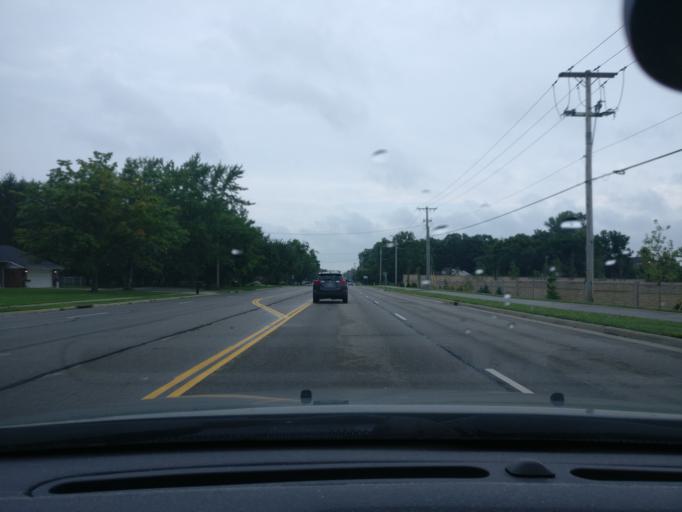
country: US
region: Ohio
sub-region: Montgomery County
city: West Carrollton City
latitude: 39.6233
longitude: -84.2359
